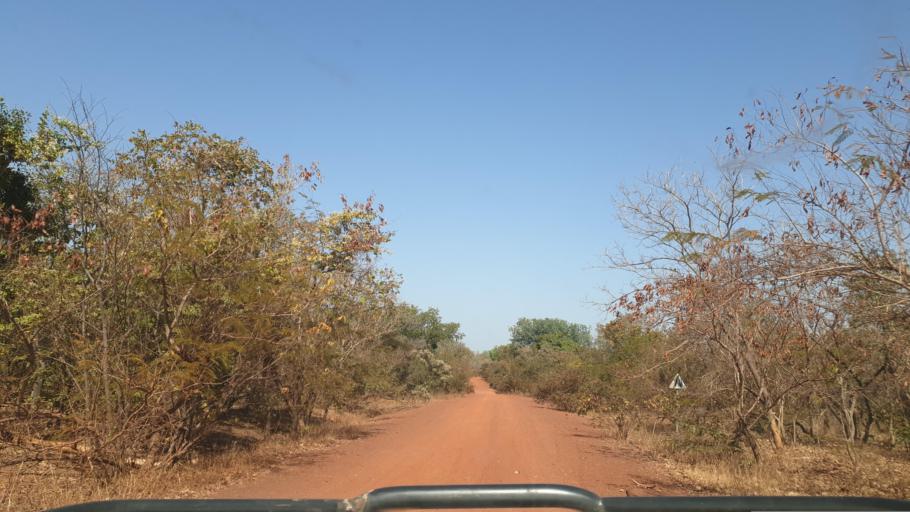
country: ML
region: Koulikoro
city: Dioila
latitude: 11.9226
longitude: -6.9840
